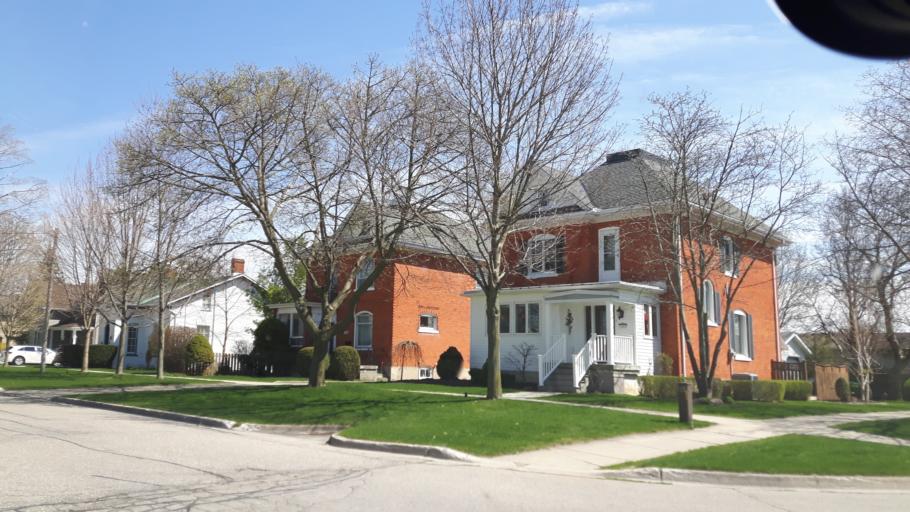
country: CA
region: Ontario
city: Goderich
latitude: 43.7431
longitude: -81.7046
